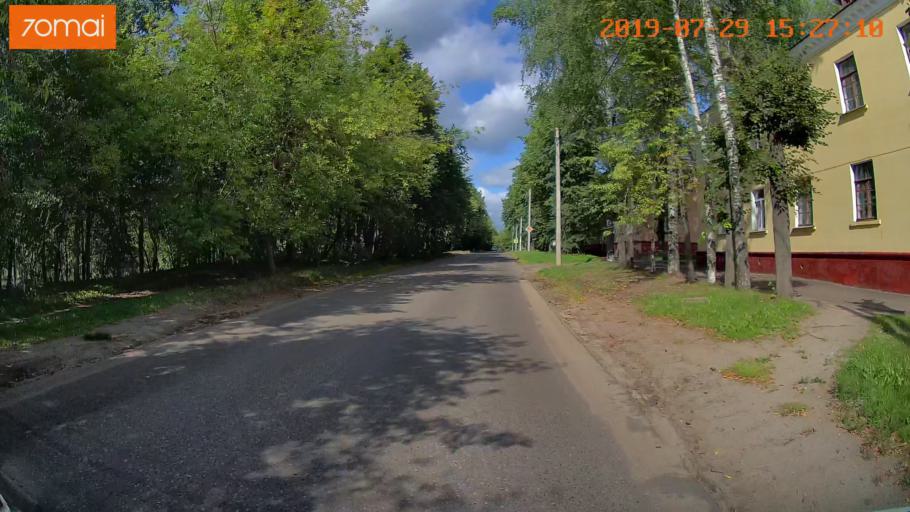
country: RU
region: Ivanovo
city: Bogorodskoye
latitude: 57.0206
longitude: 41.0058
